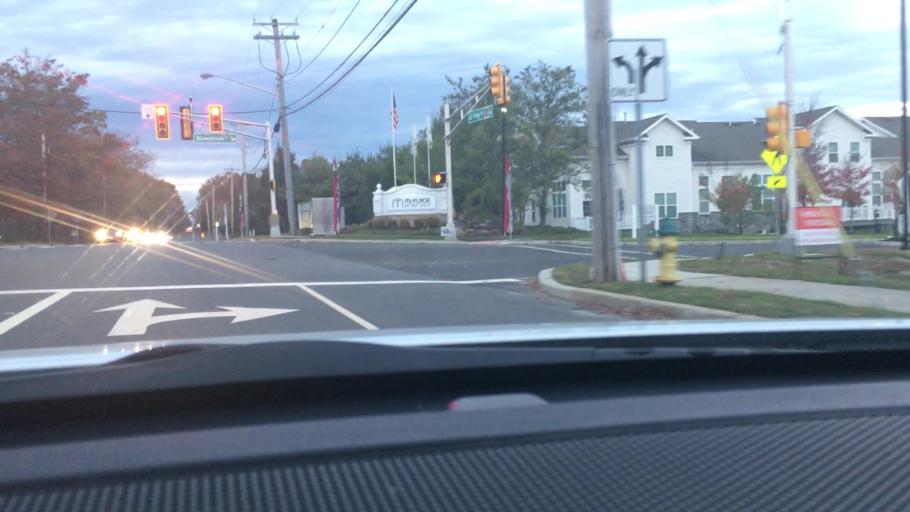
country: US
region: New Jersey
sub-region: Atlantic County
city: Absecon
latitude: 39.4395
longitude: -74.4980
